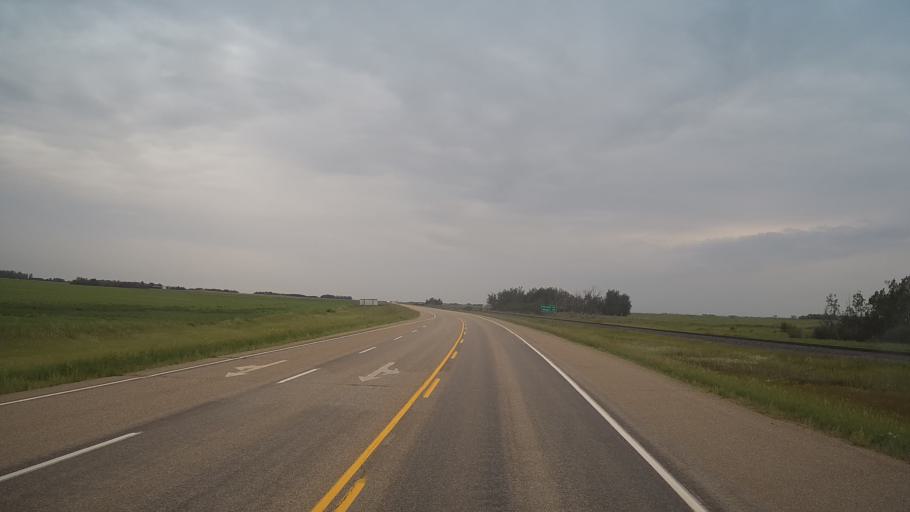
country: CA
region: Saskatchewan
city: Langham
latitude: 52.1259
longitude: -107.2902
